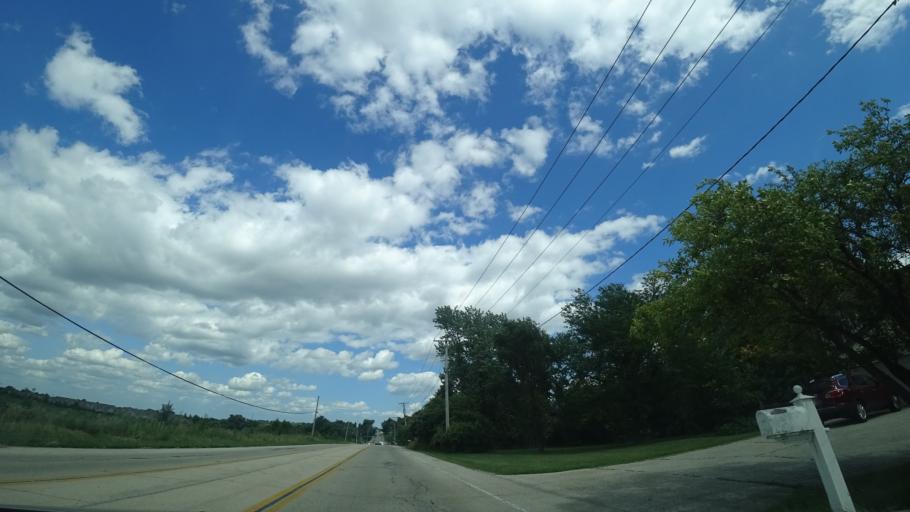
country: US
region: Illinois
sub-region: Will County
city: Homer Glen
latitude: 41.5861
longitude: -87.8953
